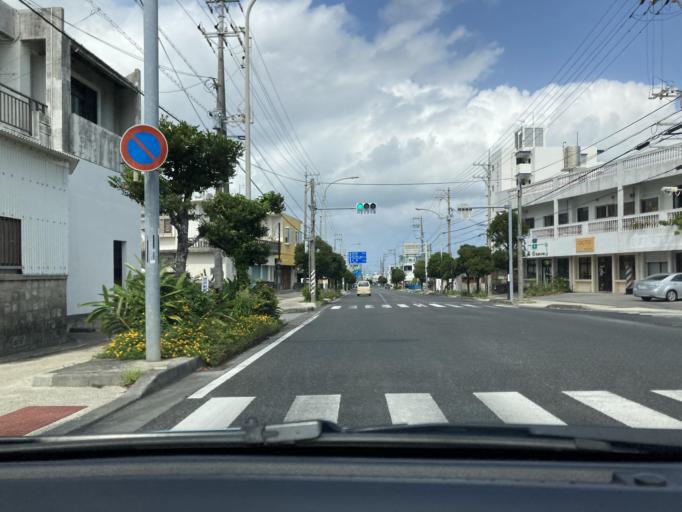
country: JP
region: Okinawa
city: Ishikawa
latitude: 26.4087
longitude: 127.8287
